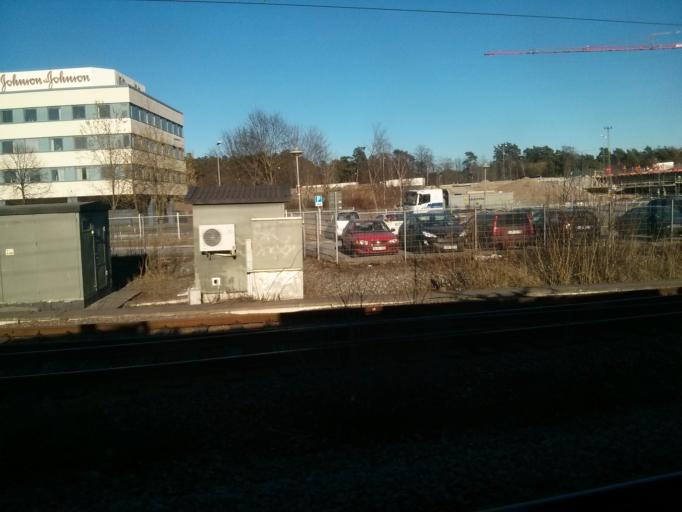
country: SE
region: Stockholm
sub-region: Upplands Vasby Kommun
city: Upplands Vaesby
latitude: 59.4762
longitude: 17.9148
